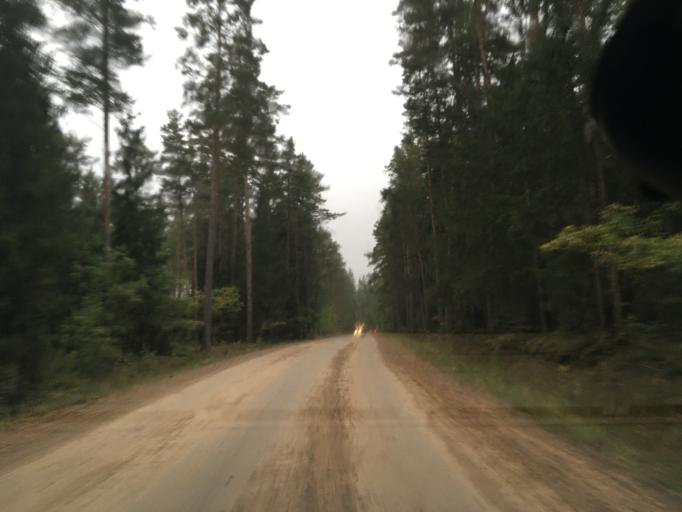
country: LV
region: Kuldigas Rajons
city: Kuldiga
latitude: 56.9913
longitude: 21.9741
